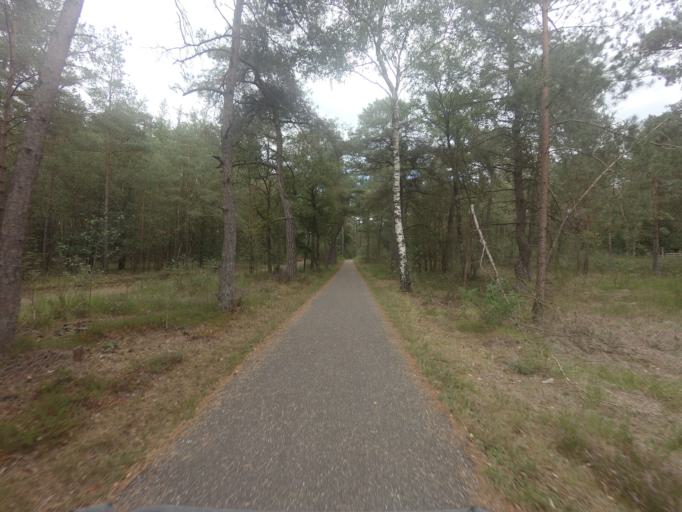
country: NL
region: Friesland
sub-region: Gemeente Weststellingwerf
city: Noordwolde
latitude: 52.9008
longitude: 6.2415
